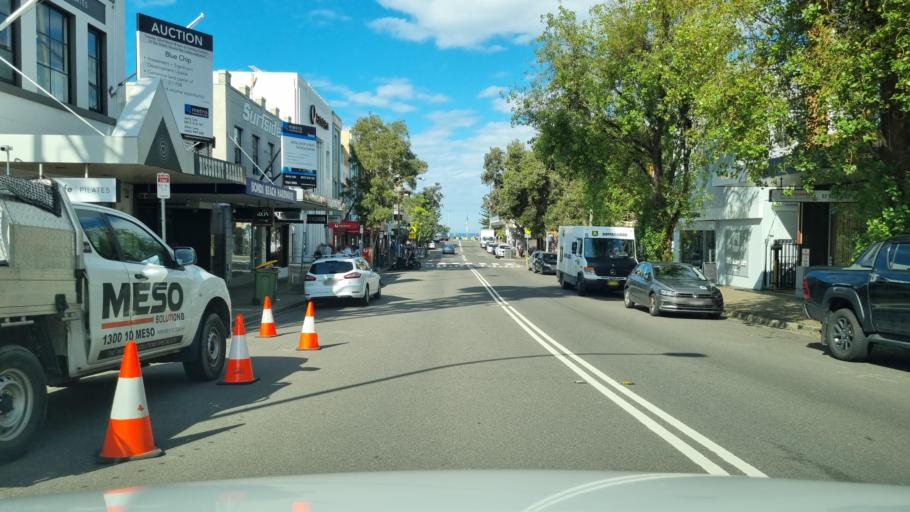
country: AU
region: New South Wales
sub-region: Waverley
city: Bondi Beach
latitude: -33.8903
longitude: 151.2725
